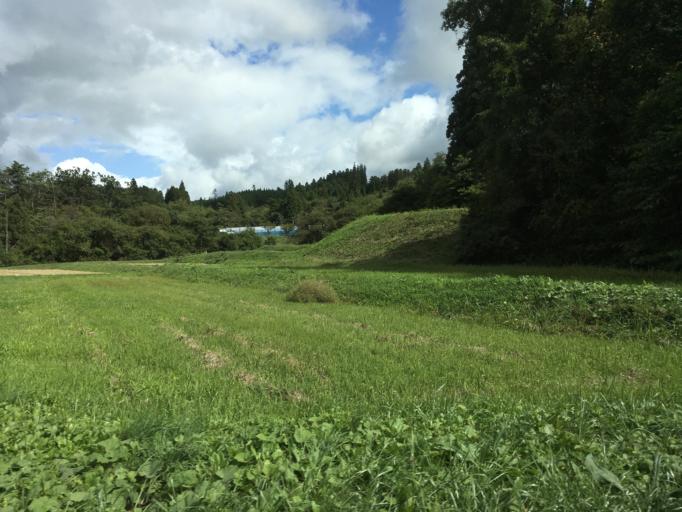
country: JP
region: Iwate
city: Ichinoseki
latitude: 38.8324
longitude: 141.3593
